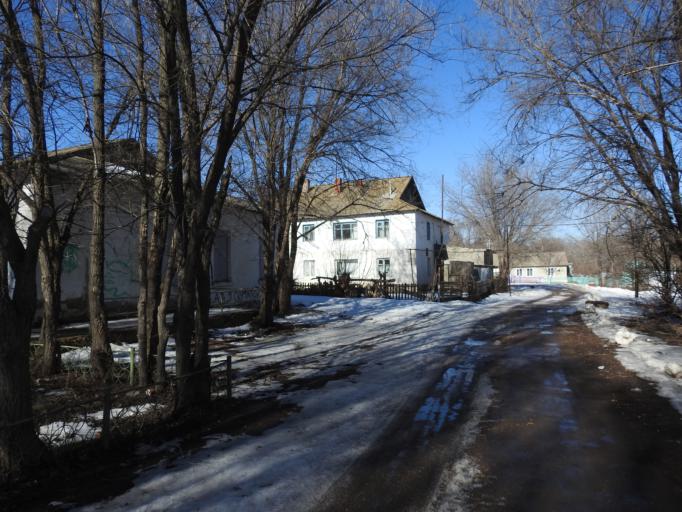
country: RU
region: Saratov
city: Yershov
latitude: 51.3407
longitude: 48.2244
